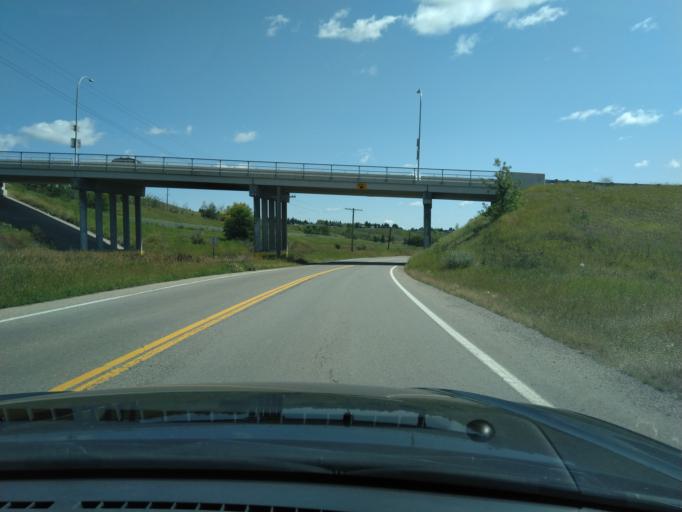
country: CA
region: Alberta
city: Calgary
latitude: 51.1013
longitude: -114.2108
